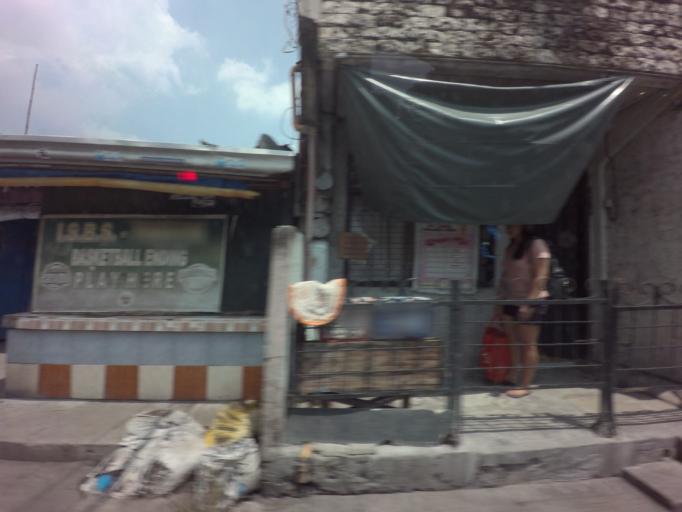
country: PH
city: Sambayanihan People's Village
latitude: 14.4388
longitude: 121.0504
